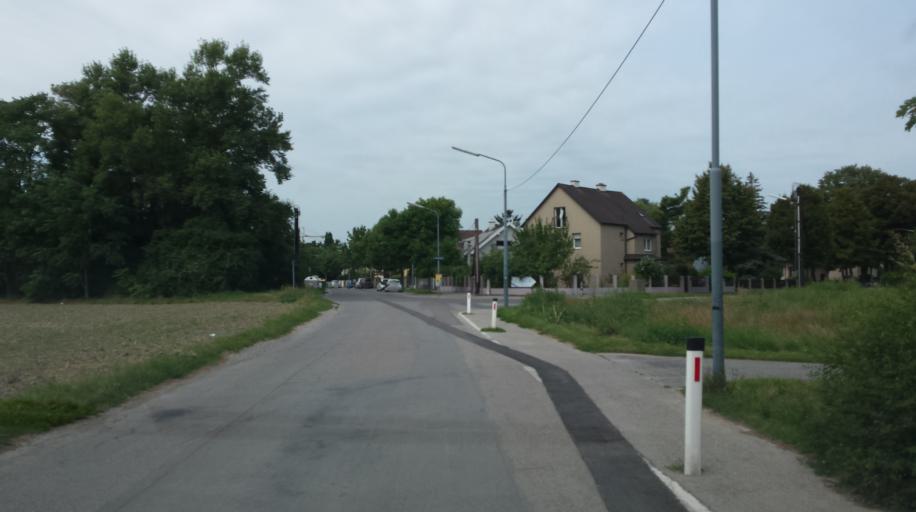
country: AT
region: Lower Austria
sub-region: Politischer Bezirk Wien-Umgebung
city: Gerasdorf bei Wien
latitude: 48.2576
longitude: 16.4266
